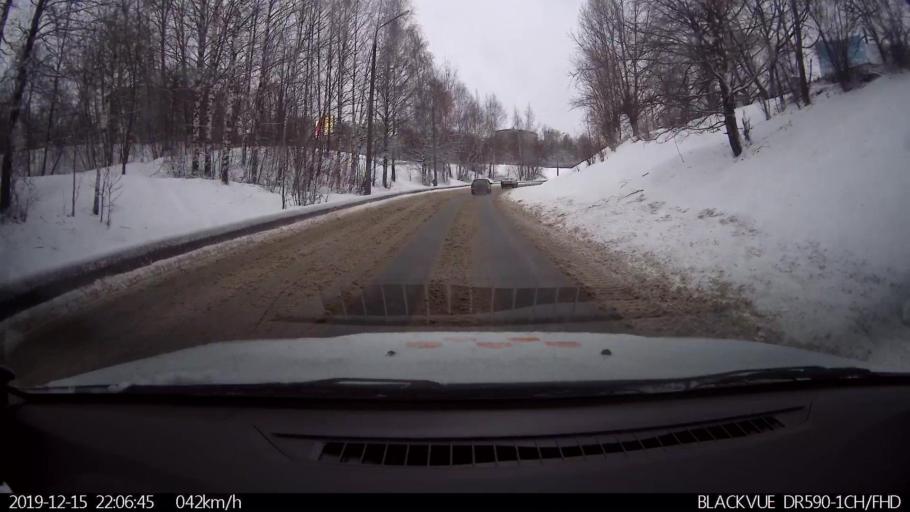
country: RU
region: Nizjnij Novgorod
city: Nizhniy Novgorod
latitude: 56.2416
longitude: 43.9620
